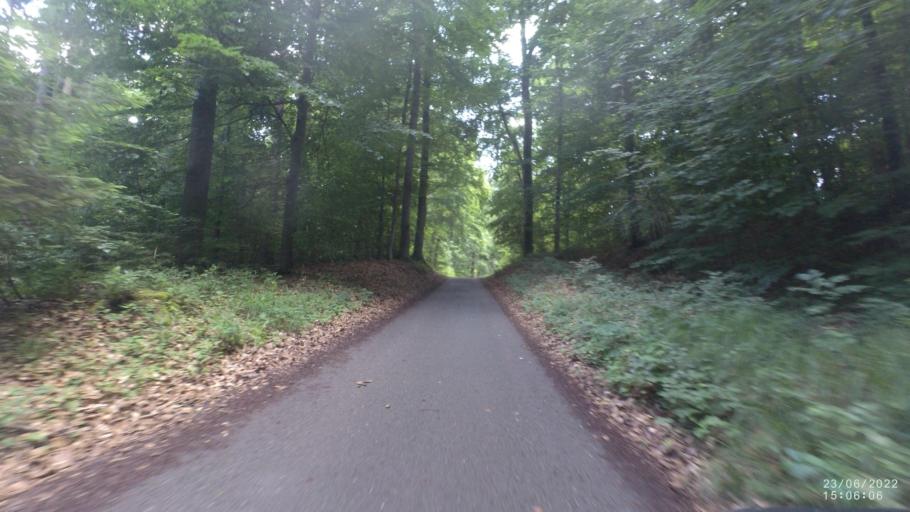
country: DE
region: Baden-Wuerttemberg
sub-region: Regierungsbezirk Stuttgart
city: Fellbach
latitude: 48.7906
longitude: 9.2931
